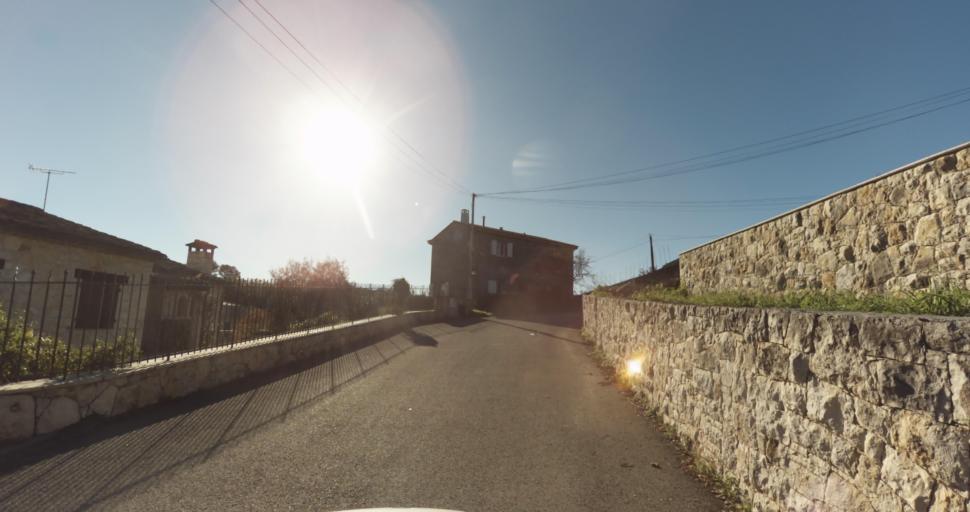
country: FR
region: Provence-Alpes-Cote d'Azur
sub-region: Departement des Alpes-Maritimes
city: Vence
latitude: 43.7182
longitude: 7.0890
